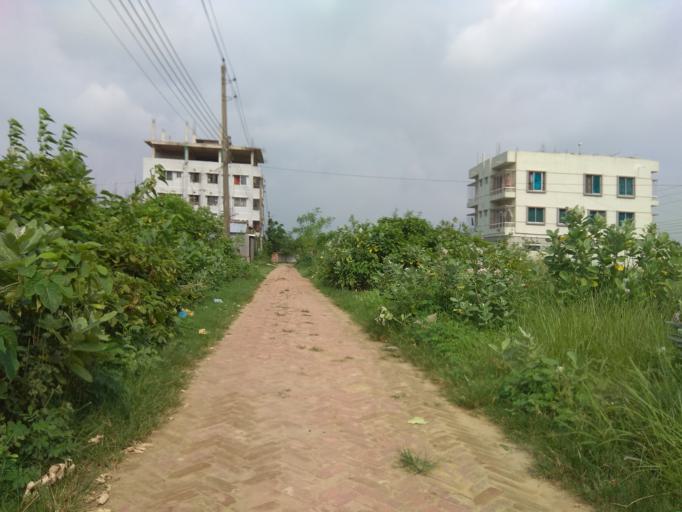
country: BD
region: Dhaka
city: Tungi
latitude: 23.8311
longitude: 90.3493
